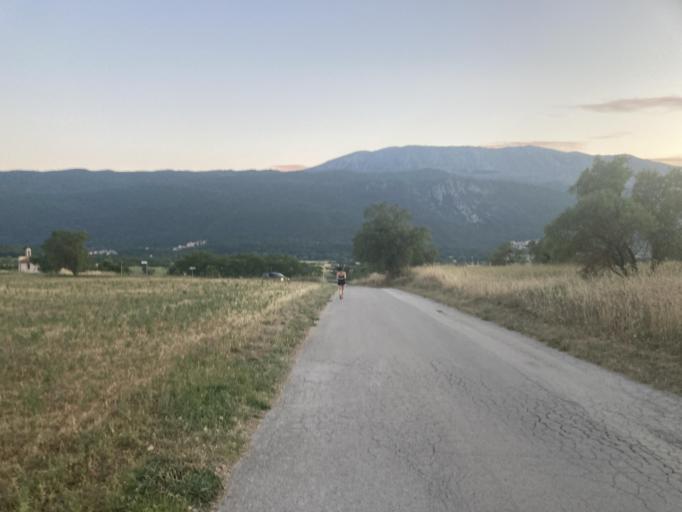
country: IT
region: Abruzzo
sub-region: Provincia dell' Aquila
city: San Demetrio Ne' Vestini
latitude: 42.2944
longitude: 13.5527
